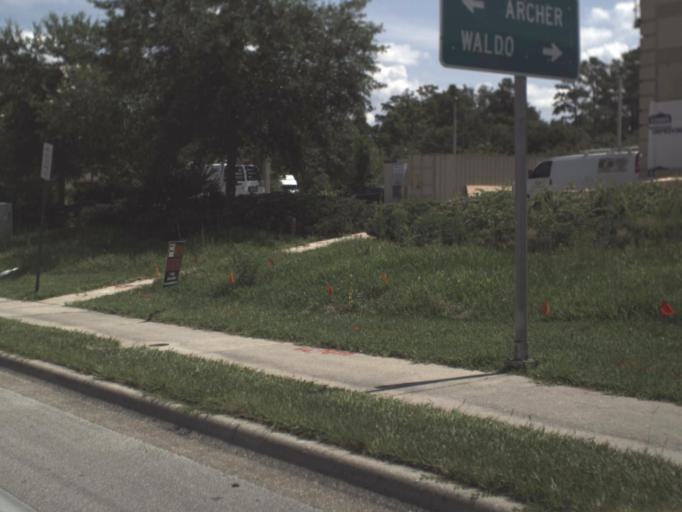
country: US
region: Florida
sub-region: Alachua County
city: Gainesville
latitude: 29.6249
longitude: -82.3723
